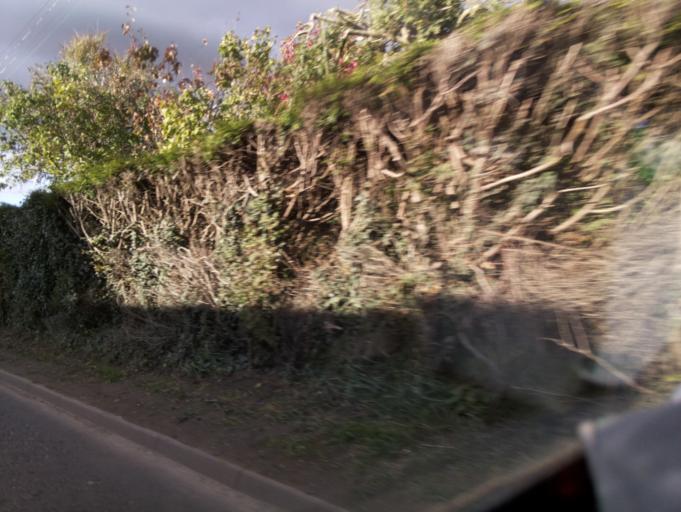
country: GB
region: England
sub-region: Herefordshire
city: Credenhill
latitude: 52.0716
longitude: -2.7799
